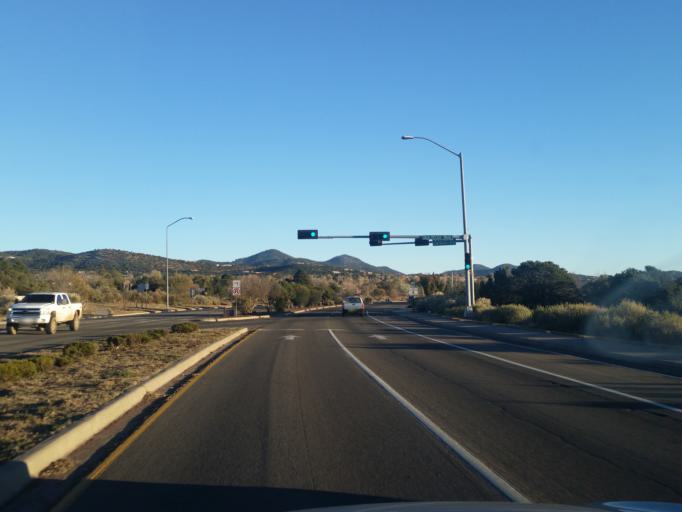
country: US
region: New Mexico
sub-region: Santa Fe County
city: Santa Fe
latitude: 35.6548
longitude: -105.9392
